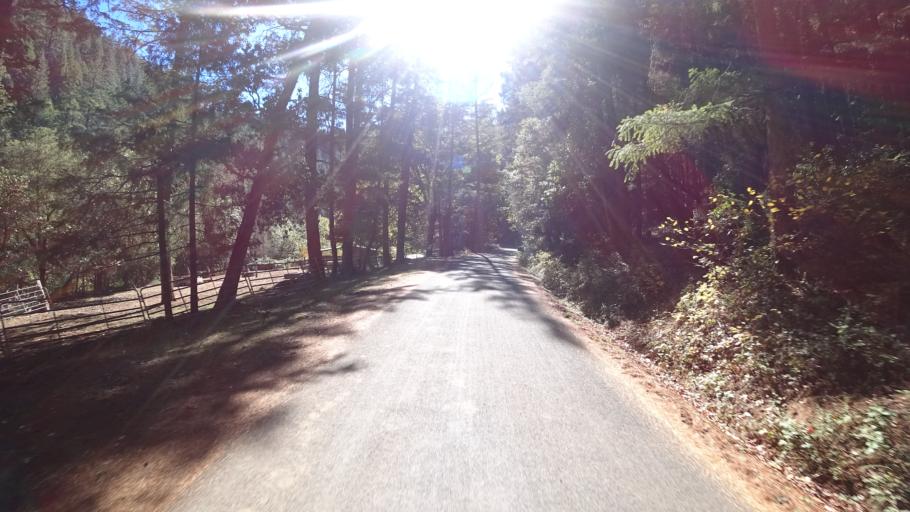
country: US
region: California
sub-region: Siskiyou County
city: Happy Camp
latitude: 41.3176
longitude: -123.1788
